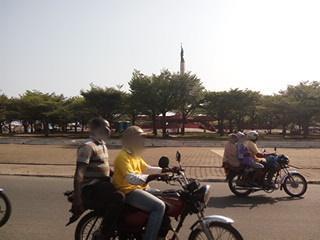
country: BJ
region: Littoral
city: Cotonou
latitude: 6.3721
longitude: 2.4101
